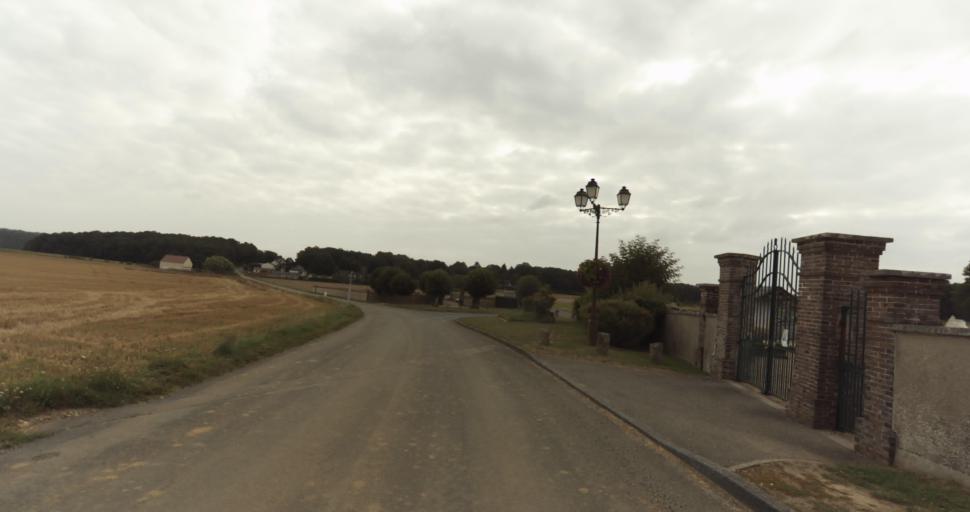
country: FR
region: Haute-Normandie
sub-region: Departement de l'Eure
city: Croth
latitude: 48.8684
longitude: 1.3508
